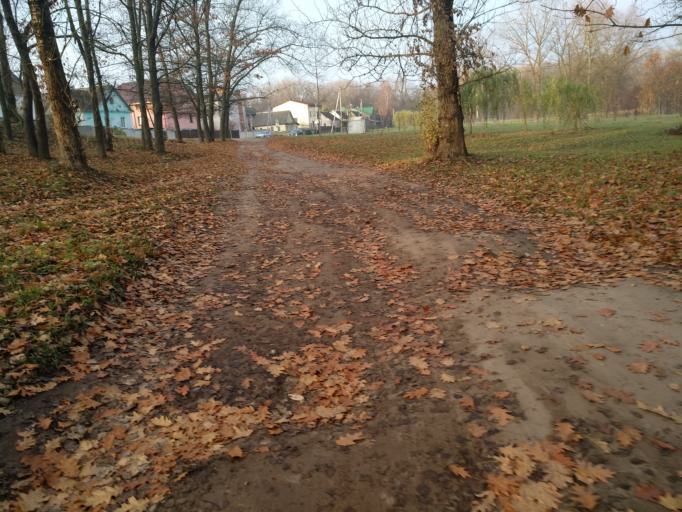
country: BY
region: Minsk
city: Minsk
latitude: 53.9410
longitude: 27.5611
